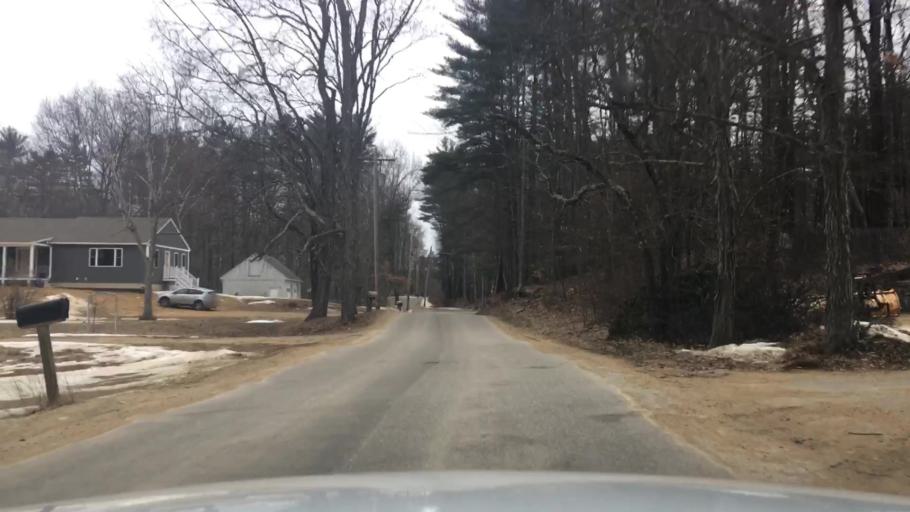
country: US
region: New Hampshire
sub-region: Strafford County
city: Rochester
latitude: 43.3446
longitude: -70.9584
